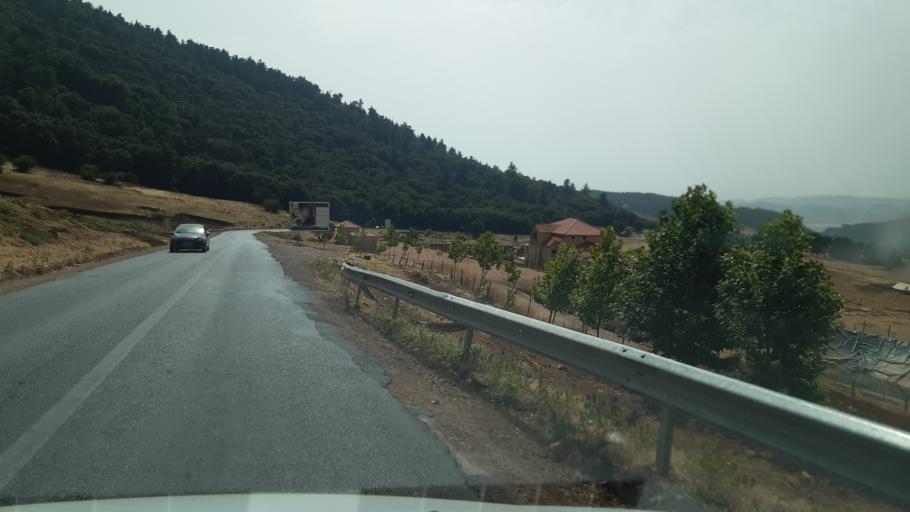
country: MA
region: Meknes-Tafilalet
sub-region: Ifrane
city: Azrou
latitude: 33.4259
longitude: -5.1929
